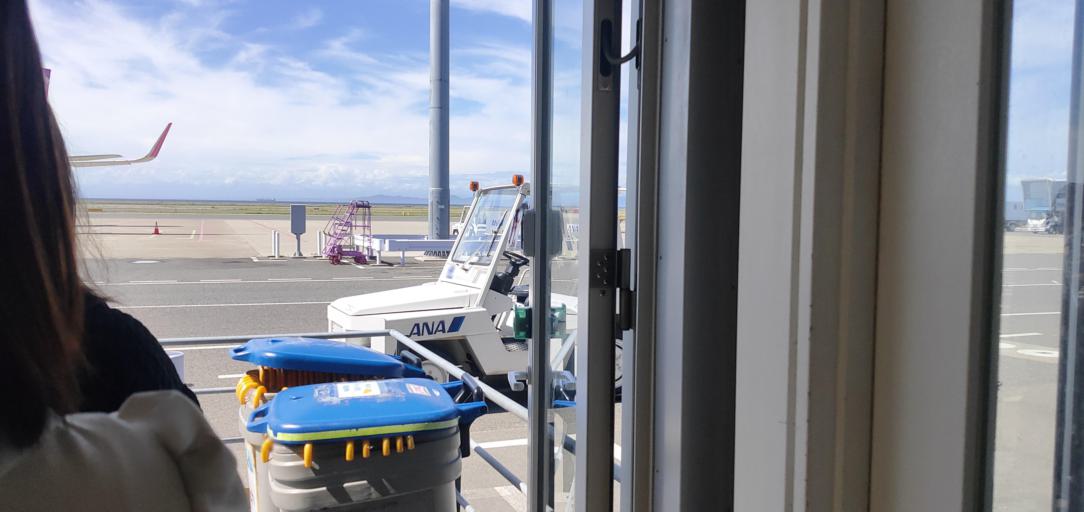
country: JP
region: Osaka
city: Kaizuka
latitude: 34.4375
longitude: 135.2296
